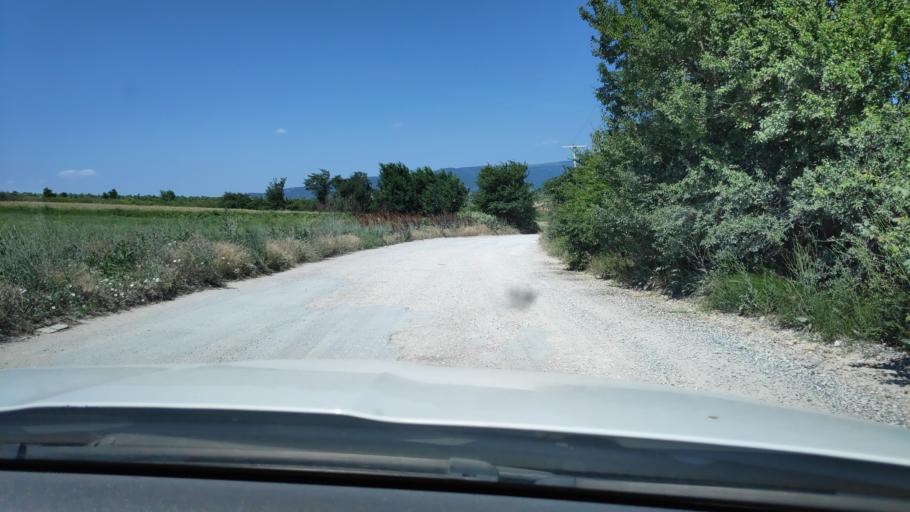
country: MK
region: Kumanovo
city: Romanovce
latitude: 42.0766
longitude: 21.7079
